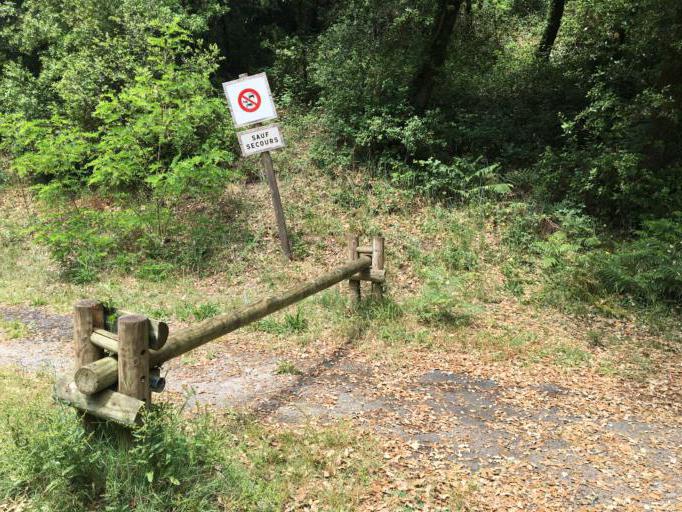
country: FR
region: Poitou-Charentes
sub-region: Departement de la Charente-Maritime
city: Meschers-sur-Gironde
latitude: 45.5872
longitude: -0.9749
